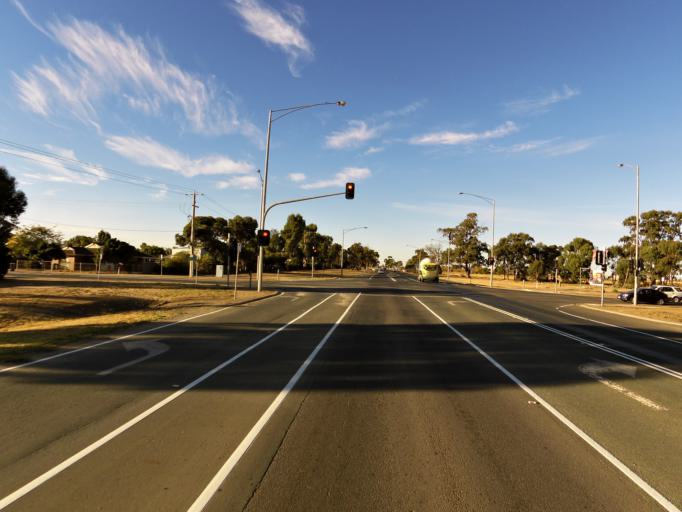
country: AU
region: Victoria
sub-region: Campaspe
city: Echuca
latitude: -36.1329
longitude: 144.7288
